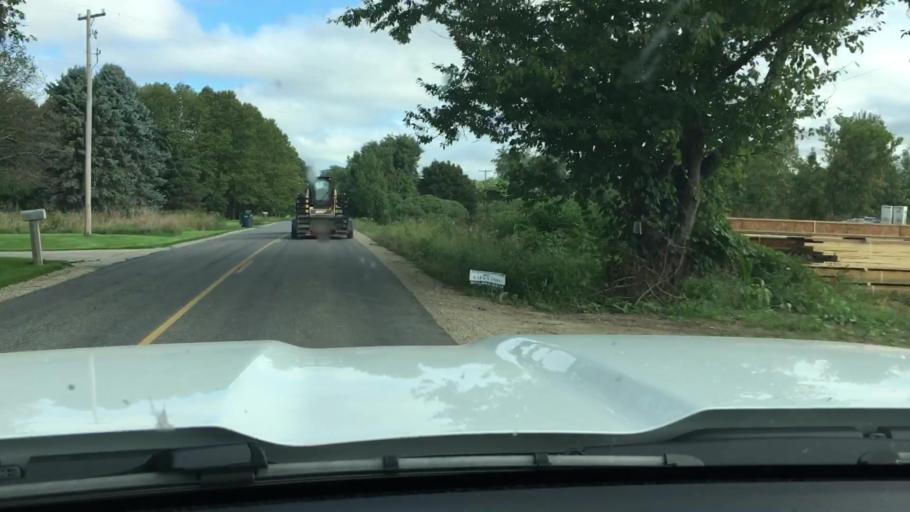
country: US
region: Michigan
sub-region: Kent County
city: Byron Center
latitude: 42.7984
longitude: -85.8027
